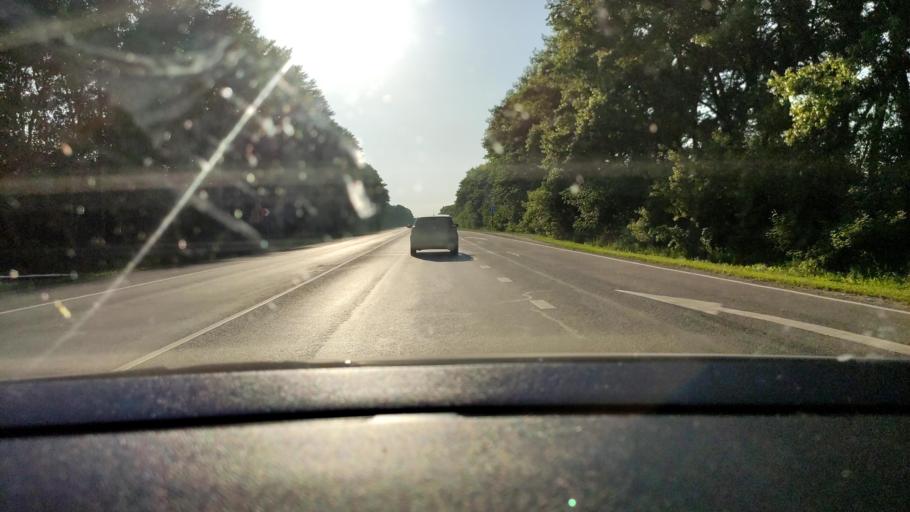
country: RU
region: Voronezj
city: Kashirskoye
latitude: 51.4929
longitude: 39.6082
